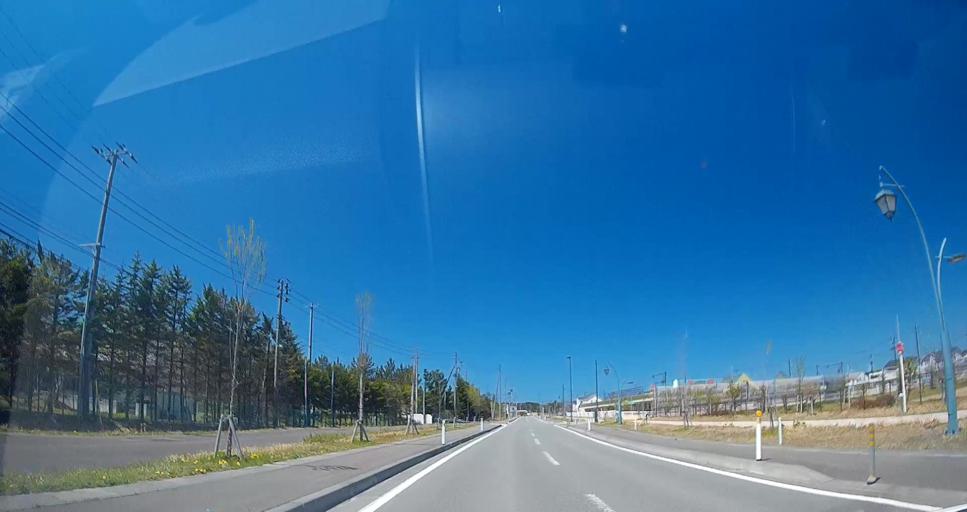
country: JP
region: Aomori
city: Misawa
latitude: 40.9686
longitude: 141.3665
